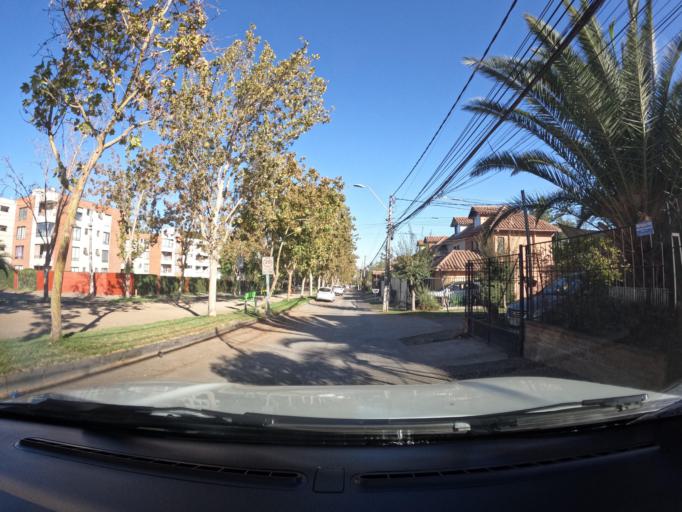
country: CL
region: Santiago Metropolitan
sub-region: Provincia de Santiago
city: Villa Presidente Frei, Nunoa, Santiago, Chile
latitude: -33.4754
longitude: -70.5517
